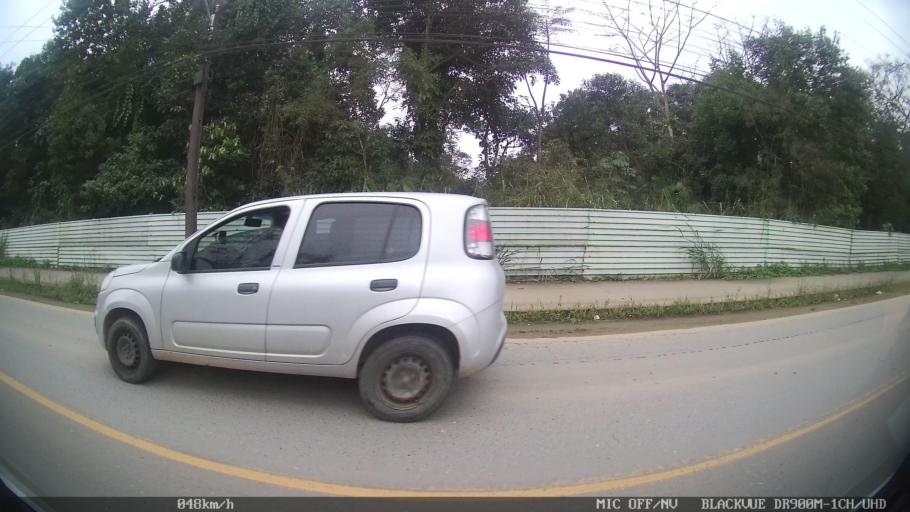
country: BR
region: Santa Catarina
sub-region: Joinville
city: Joinville
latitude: -26.2649
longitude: -48.9244
